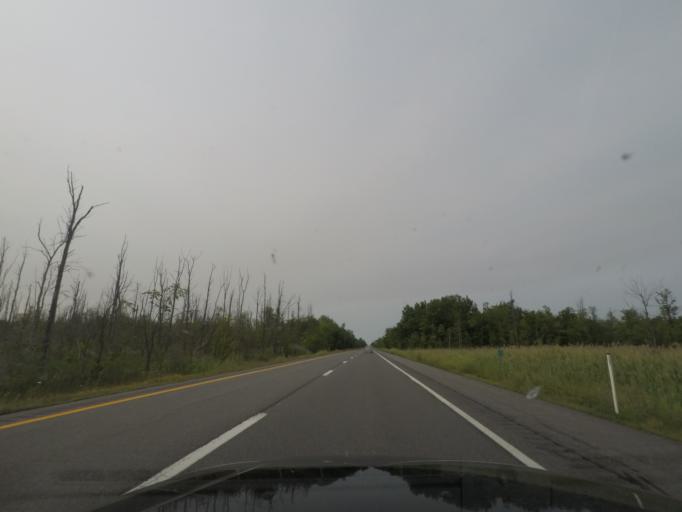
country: US
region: New York
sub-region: Clinton County
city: Champlain
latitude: 44.9432
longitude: -73.4475
